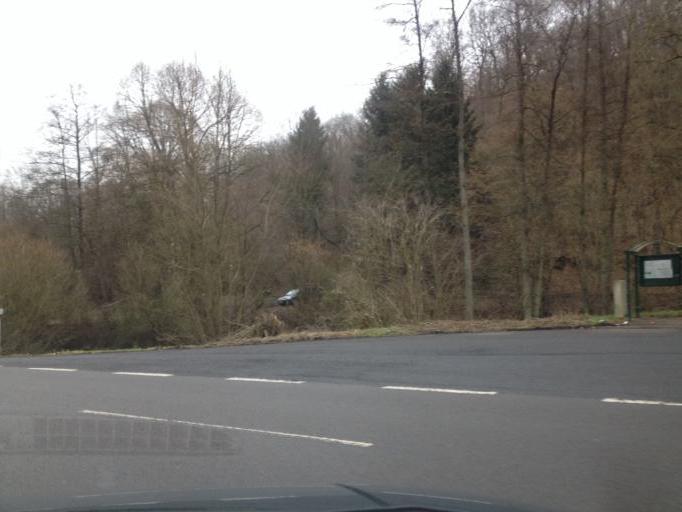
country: DE
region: Saarland
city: Hangard
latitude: 49.3958
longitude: 7.2158
